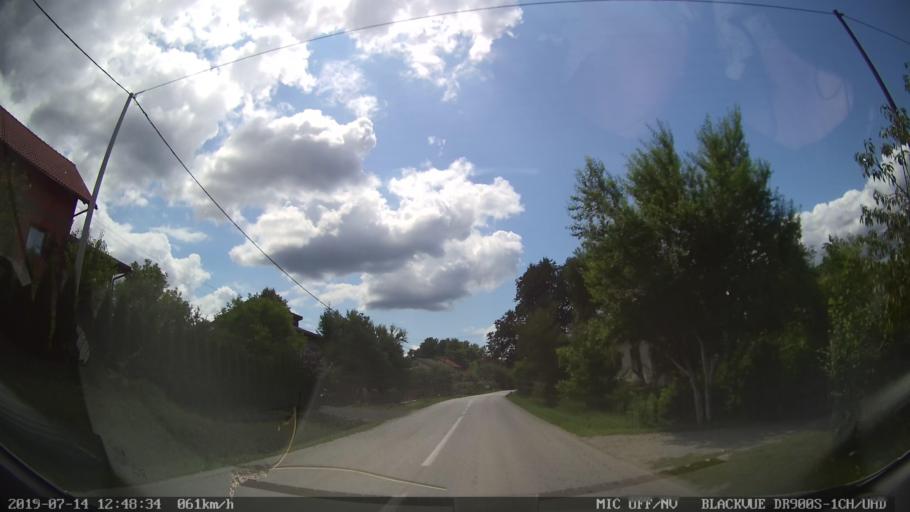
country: HR
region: Karlovacka
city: Vojnic
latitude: 45.3330
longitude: 15.6920
